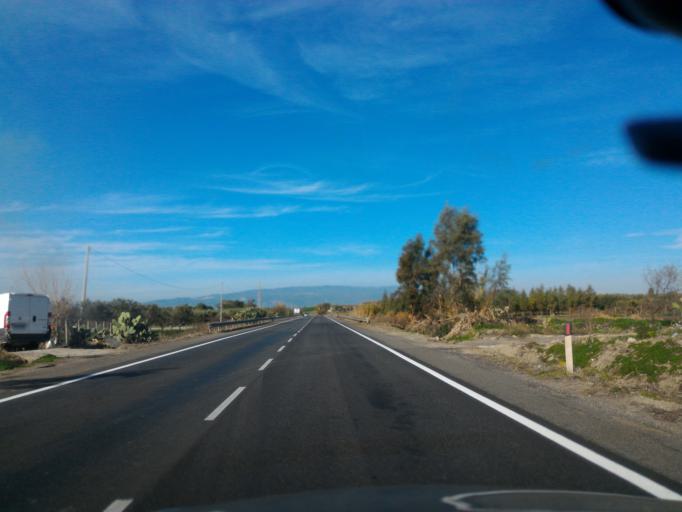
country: IT
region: Calabria
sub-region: Provincia di Crotone
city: Le Castella
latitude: 38.9356
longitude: 17.0057
